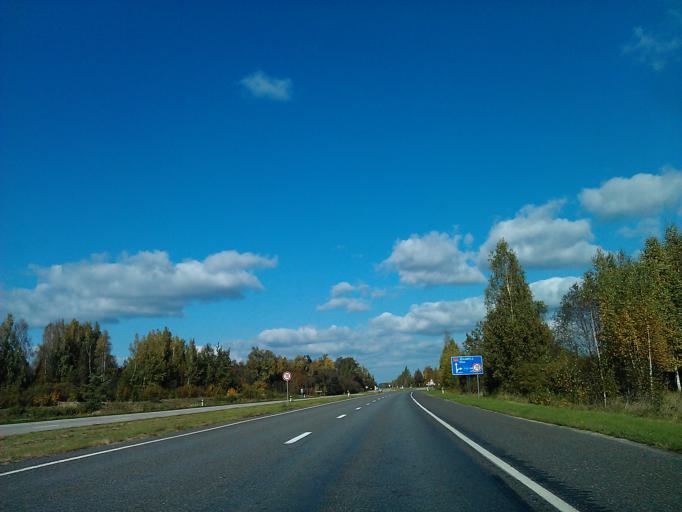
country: LV
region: Ilukste
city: Ilukste
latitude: 56.1367
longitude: 26.3434
